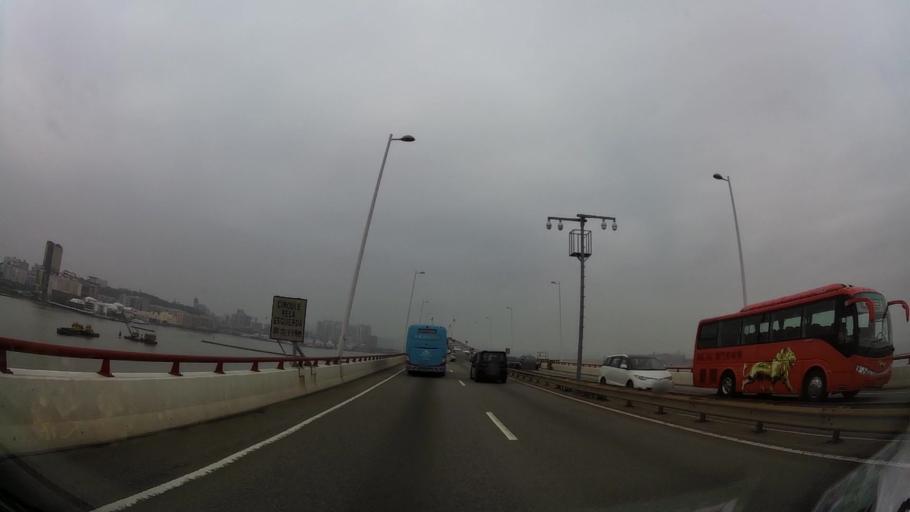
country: MO
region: Macau
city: Macau
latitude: 22.1851
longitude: 113.5632
